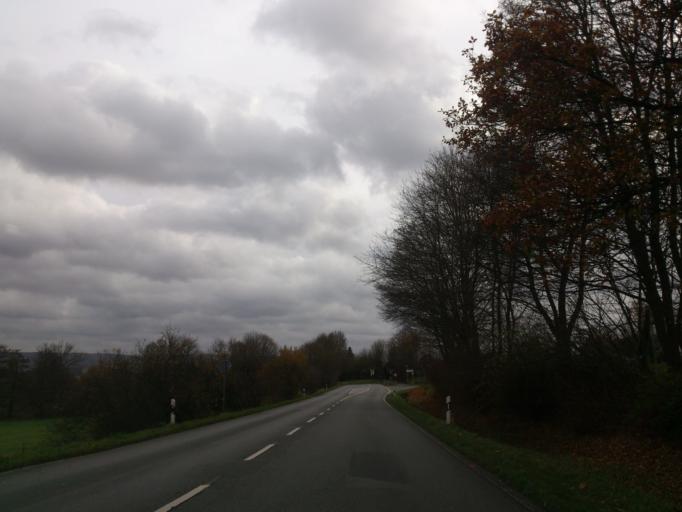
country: DE
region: North Rhine-Westphalia
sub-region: Regierungsbezirk Detmold
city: Hoexter
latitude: 51.7868
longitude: 9.3665
